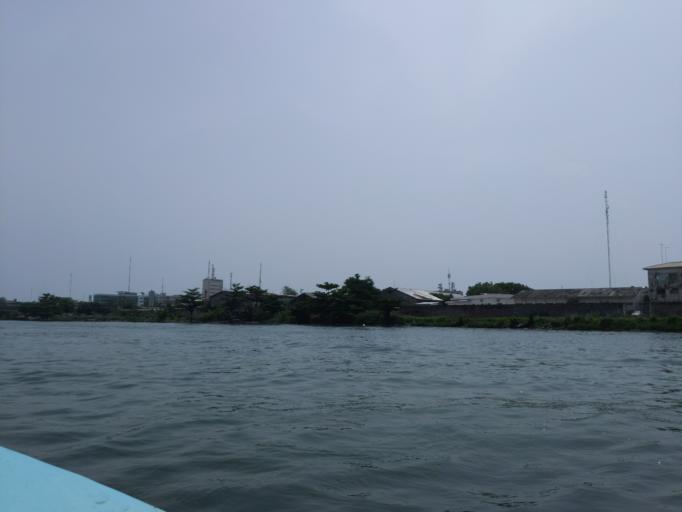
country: BJ
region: Littoral
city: Cotonou
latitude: 6.3624
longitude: 2.4396
